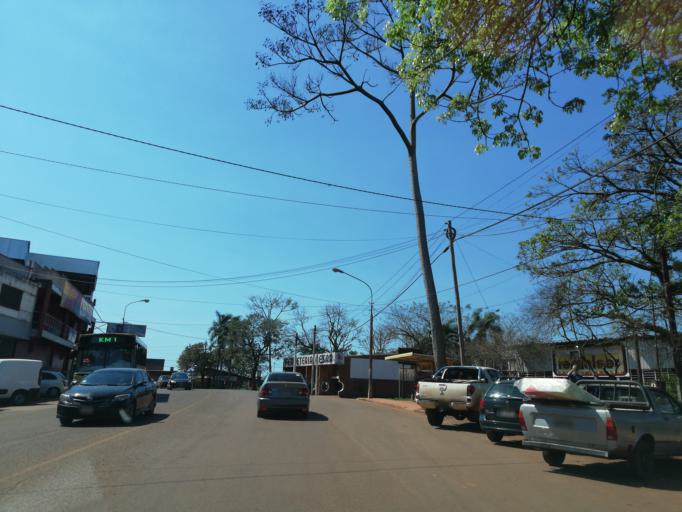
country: AR
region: Misiones
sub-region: Departamento de Eldorado
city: Eldorado
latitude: -26.4041
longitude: -54.6317
